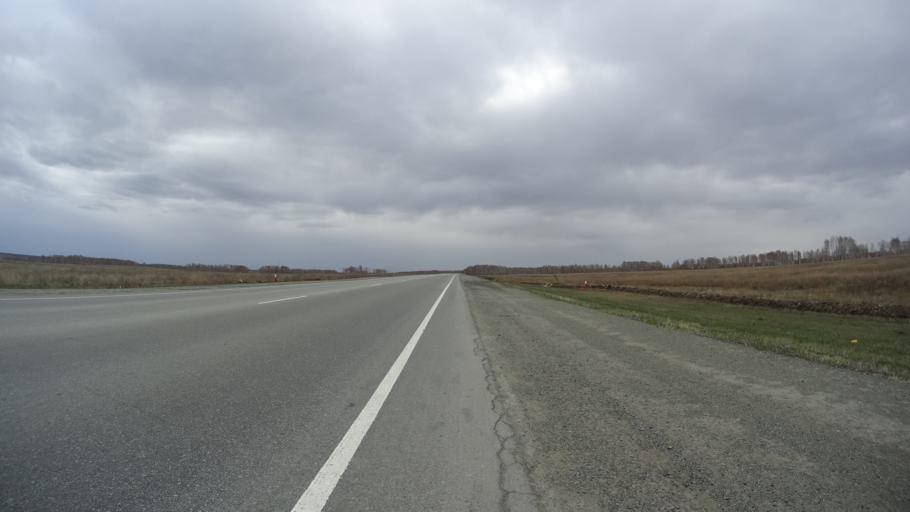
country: RU
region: Chelyabinsk
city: Yemanzhelinsk
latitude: 54.7052
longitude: 61.2560
